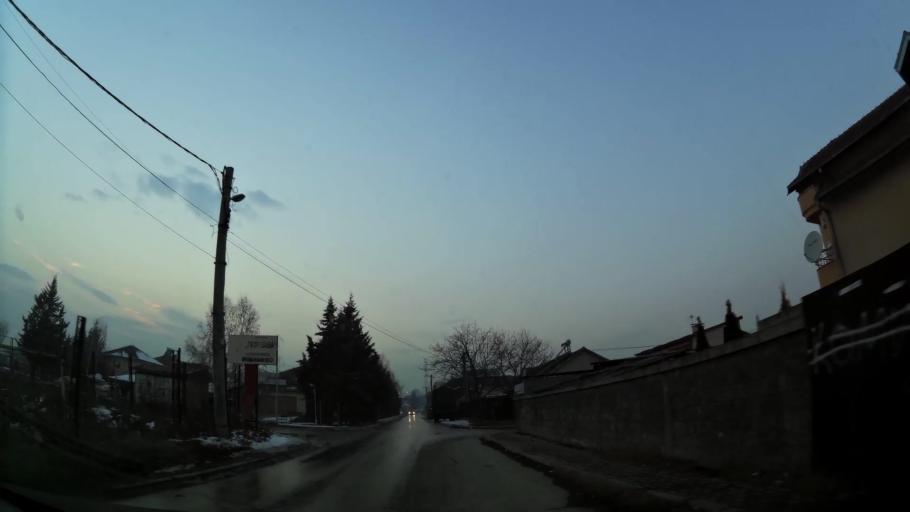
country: MK
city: Creshevo
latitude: 42.0030
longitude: 21.5064
